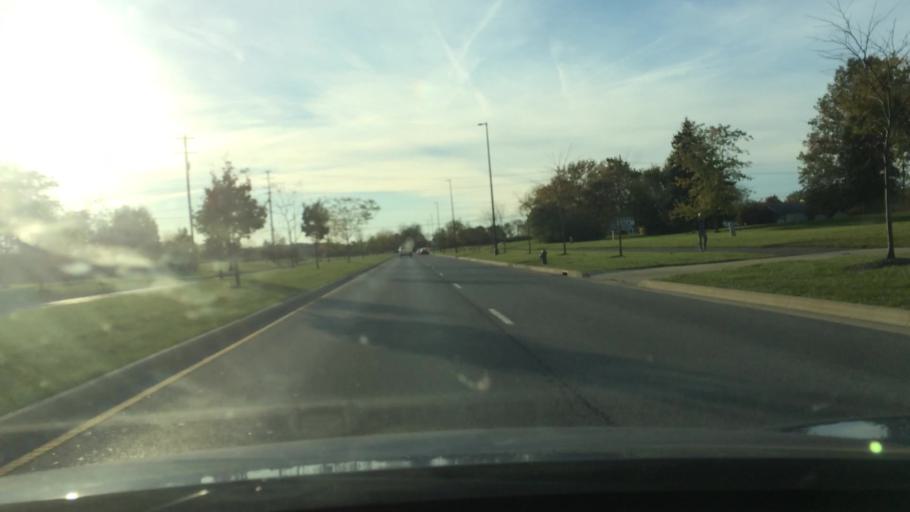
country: US
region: Ohio
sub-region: Franklin County
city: Dublin
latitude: 40.0746
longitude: -83.1462
